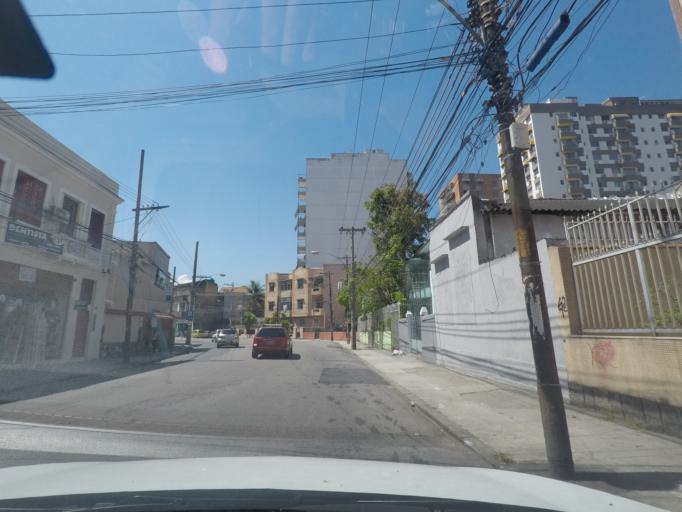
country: BR
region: Rio de Janeiro
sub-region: Rio De Janeiro
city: Rio de Janeiro
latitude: -22.9212
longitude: -43.2588
